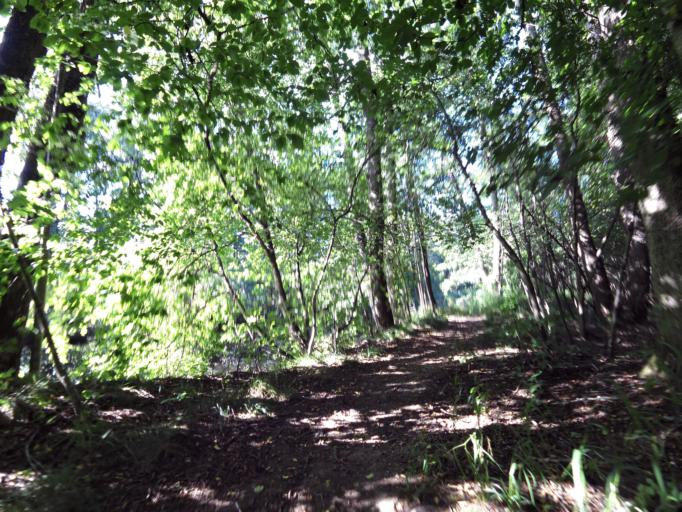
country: SE
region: Gaevleborg
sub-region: Gavle Kommun
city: Gavle
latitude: 60.7062
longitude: 17.1545
